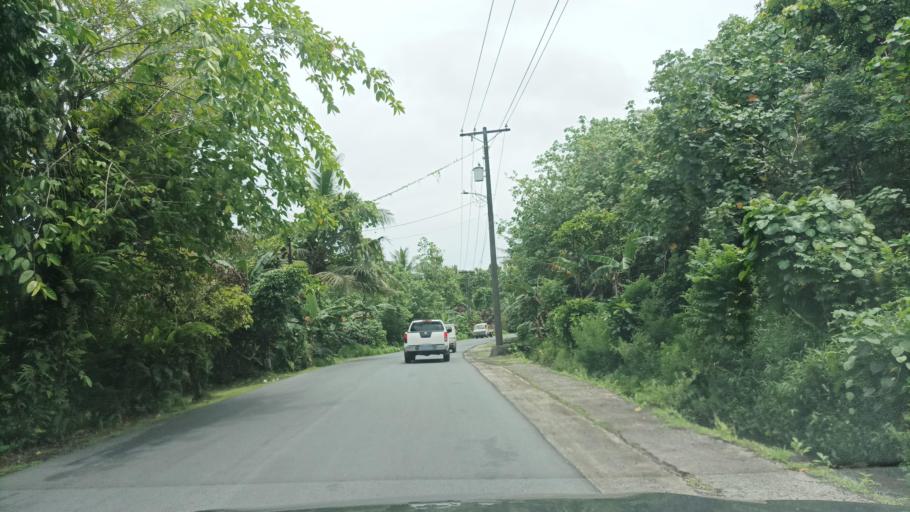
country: FM
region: Pohnpei
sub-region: Sokehs Municipality
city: Palikir - National Government Center
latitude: 6.9424
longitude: 158.1839
